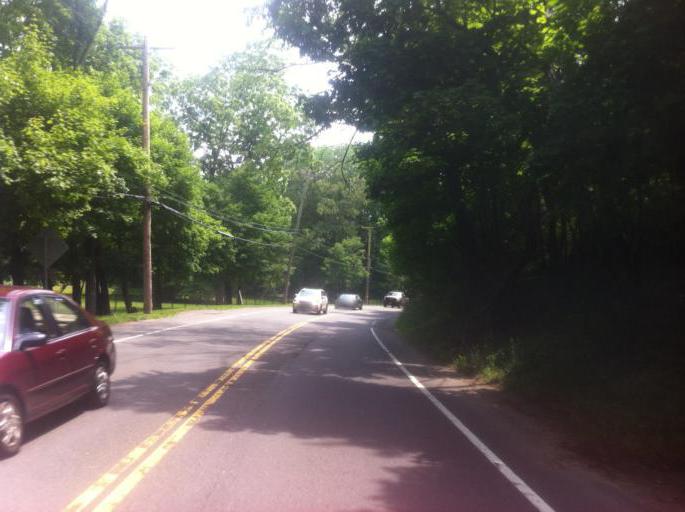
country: US
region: New York
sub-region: Nassau County
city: Old Brookville
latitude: 40.8297
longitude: -73.6029
